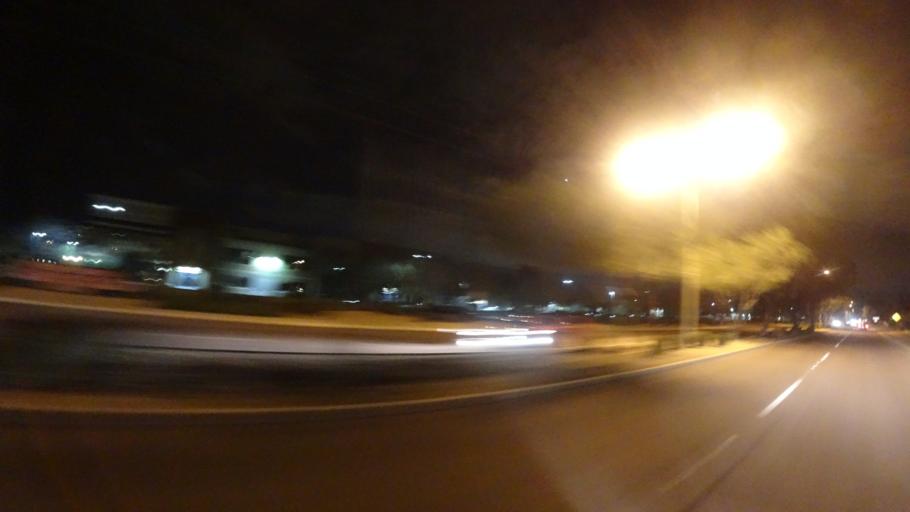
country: US
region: Arizona
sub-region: Maricopa County
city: Chandler
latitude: 33.3095
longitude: -111.9111
